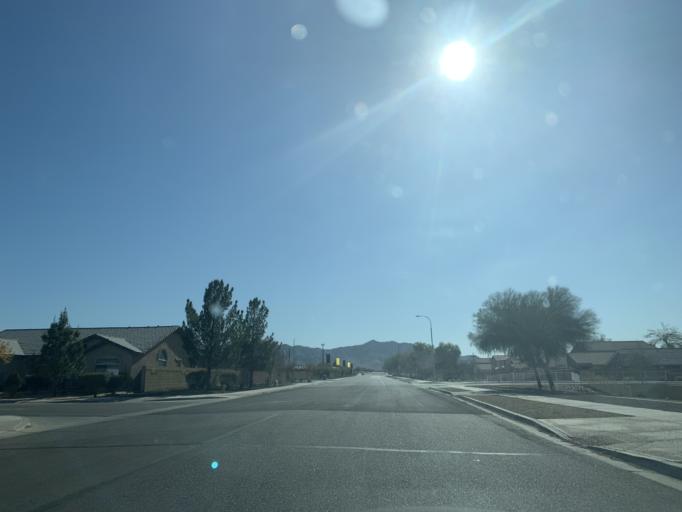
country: US
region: Arizona
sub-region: Maricopa County
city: Laveen
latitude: 33.3964
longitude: -112.1250
